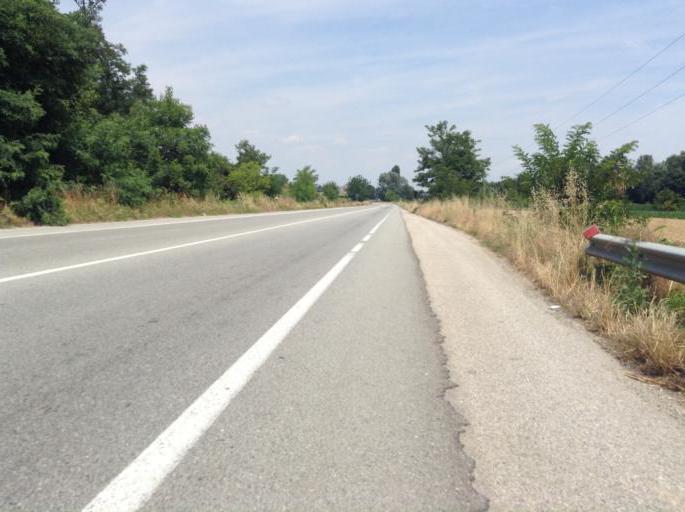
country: IT
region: Piedmont
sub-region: Provincia di Torino
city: Carignano
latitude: 44.8972
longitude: 7.6738
